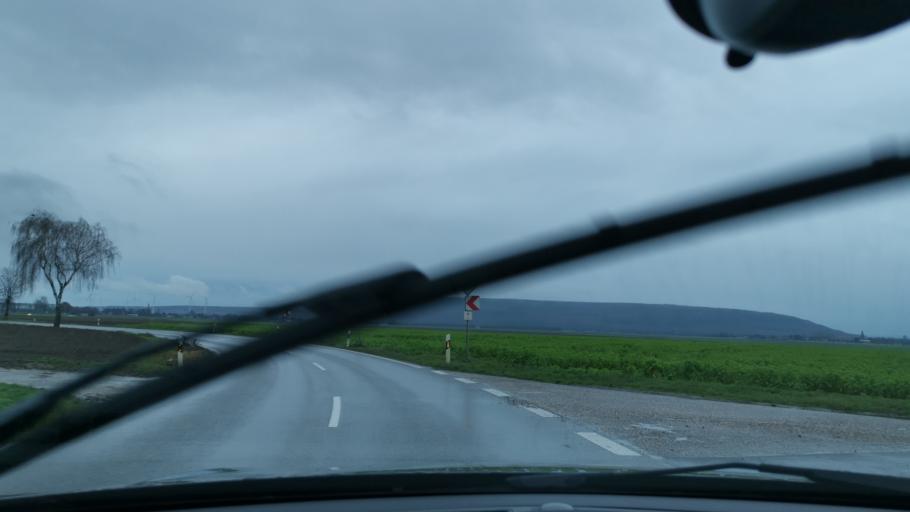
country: DE
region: North Rhine-Westphalia
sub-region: Regierungsbezirk Koln
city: Titz
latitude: 50.9813
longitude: 6.4386
